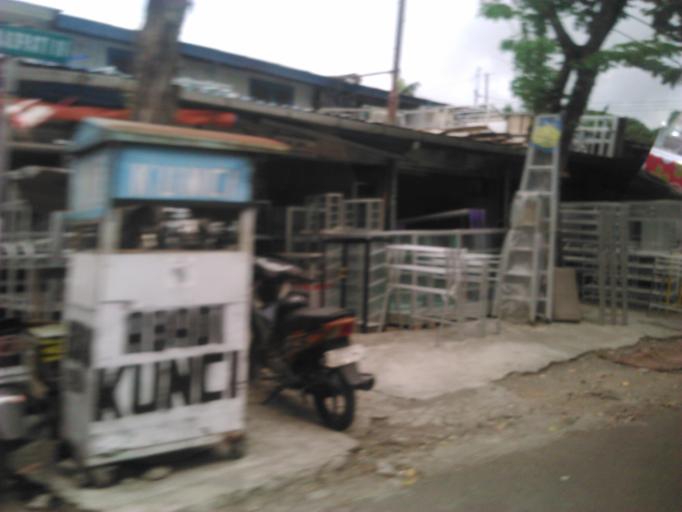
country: ID
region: East Java
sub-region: Kota Surabaya
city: Surabaya
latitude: -7.2478
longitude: 112.7331
